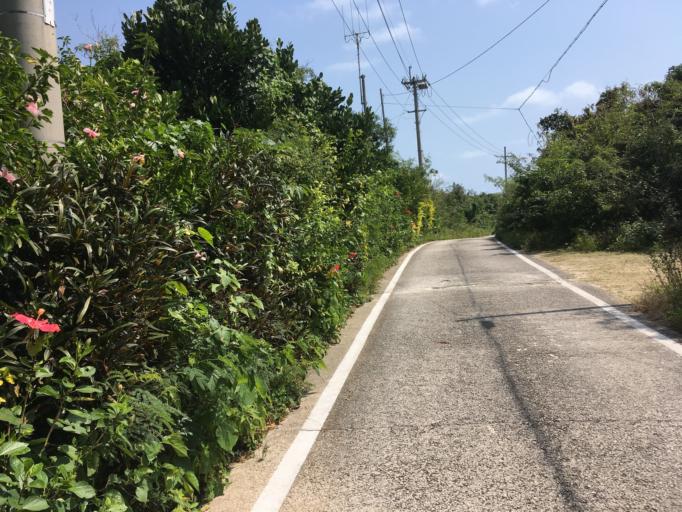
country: JP
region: Okinawa
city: Ishigaki
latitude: 24.3254
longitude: 124.0798
